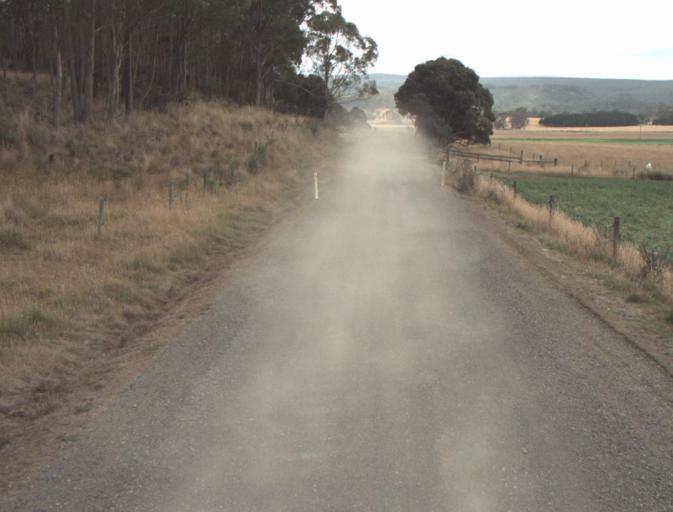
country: AU
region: Tasmania
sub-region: Northern Midlands
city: Evandale
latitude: -41.4834
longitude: 147.4413
